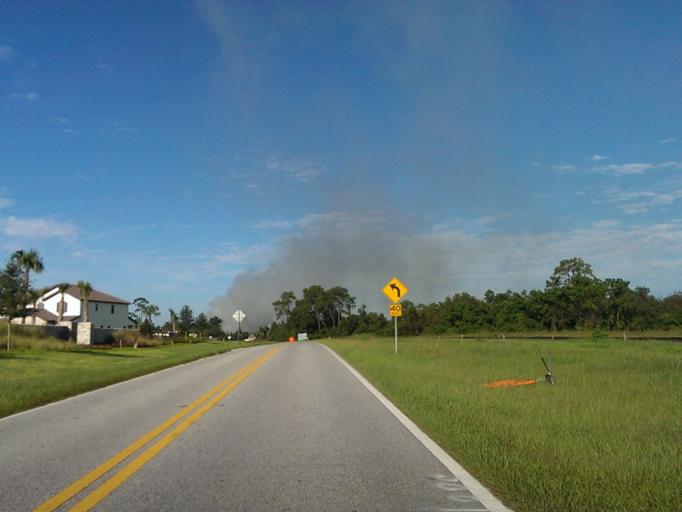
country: US
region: Florida
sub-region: Orange County
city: Lake Butler
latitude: 28.4310
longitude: -81.6128
